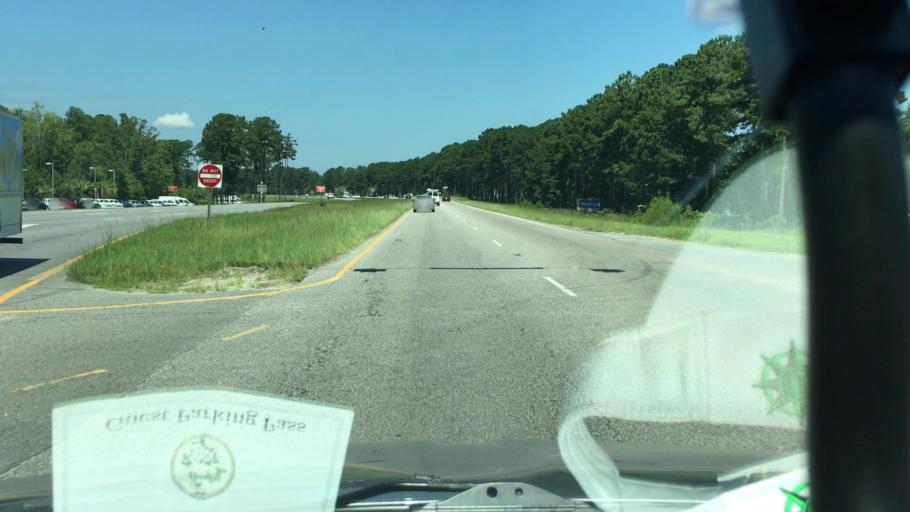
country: US
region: South Carolina
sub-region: Jasper County
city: Hardeeville
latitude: 32.3082
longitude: -80.9767
